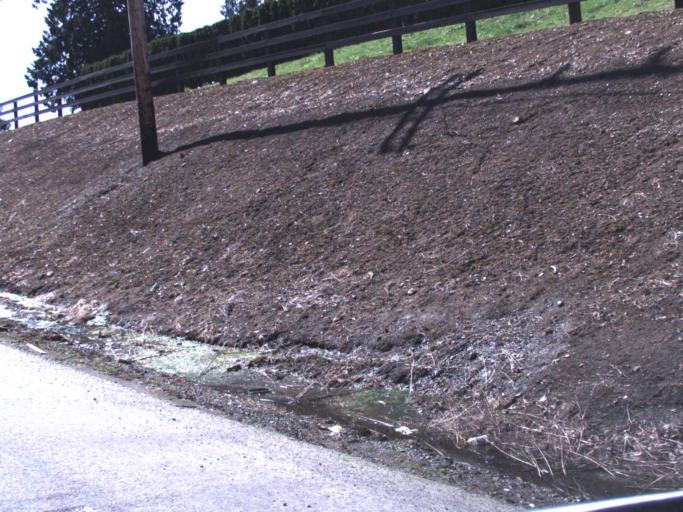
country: US
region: Washington
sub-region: King County
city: Black Diamond
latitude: 47.2585
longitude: -121.9864
